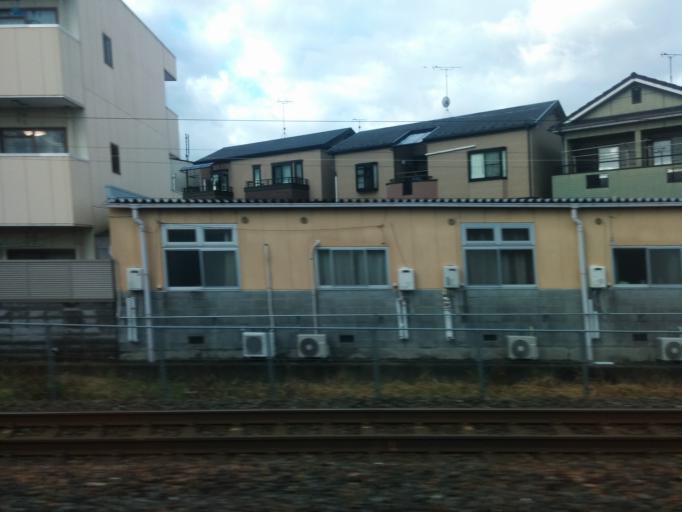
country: JP
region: Shiga Prefecture
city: Otsu-shi
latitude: 34.9900
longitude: 135.8880
